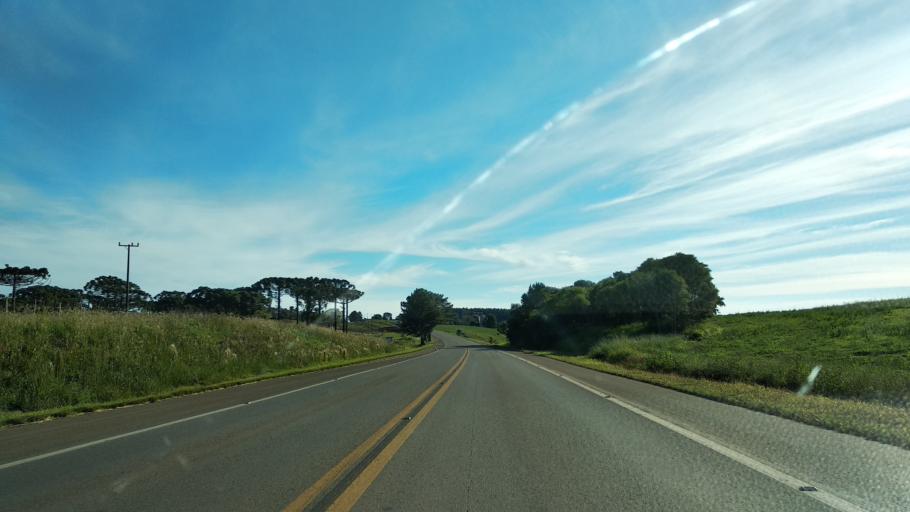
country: BR
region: Santa Catarina
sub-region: Celso Ramos
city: Celso Ramos
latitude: -27.5269
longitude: -51.3732
